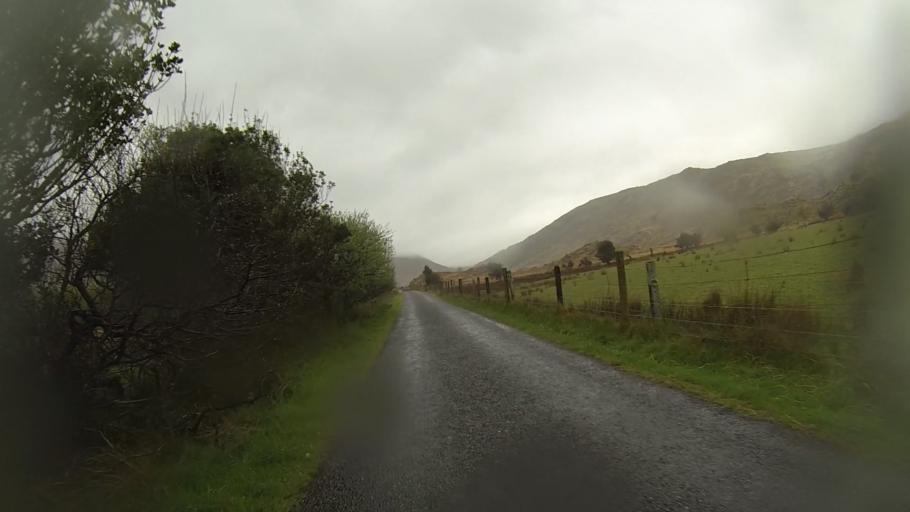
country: IE
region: Munster
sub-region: Ciarrai
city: Kenmare
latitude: 51.9496
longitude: -9.6837
